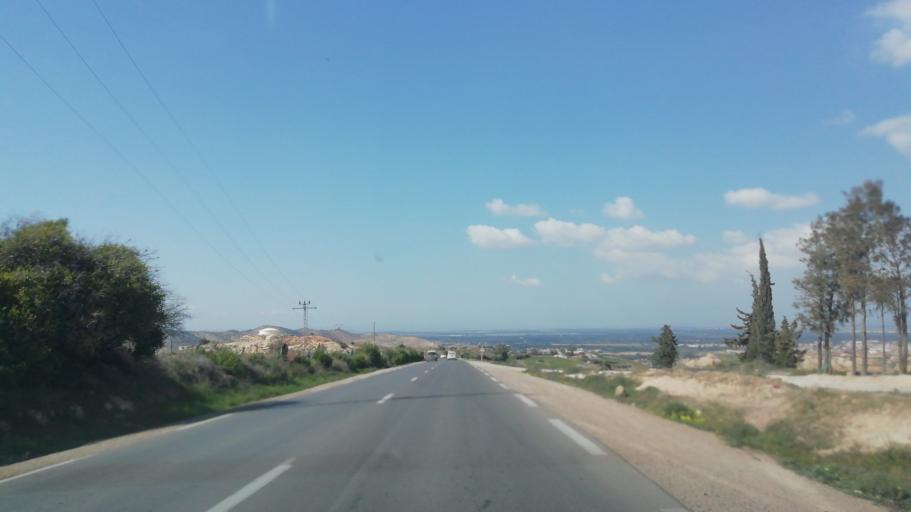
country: DZ
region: Mascara
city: Mascara
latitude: 35.5532
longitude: 0.0821
